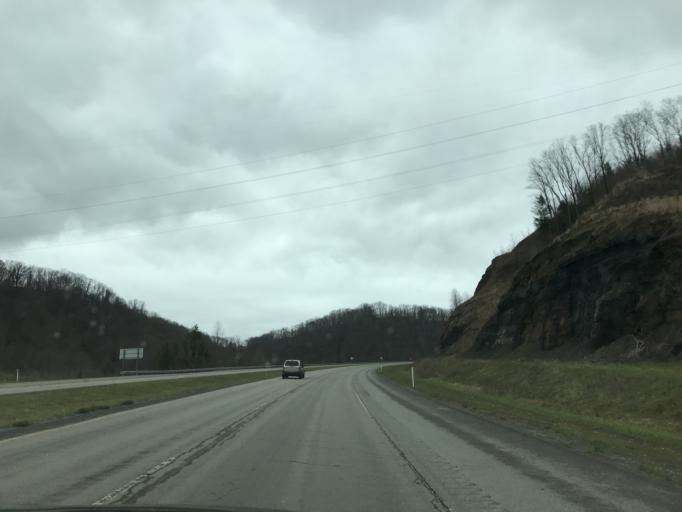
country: US
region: West Virginia
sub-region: Raleigh County
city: Sophia
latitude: 37.7016
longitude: -81.3078
